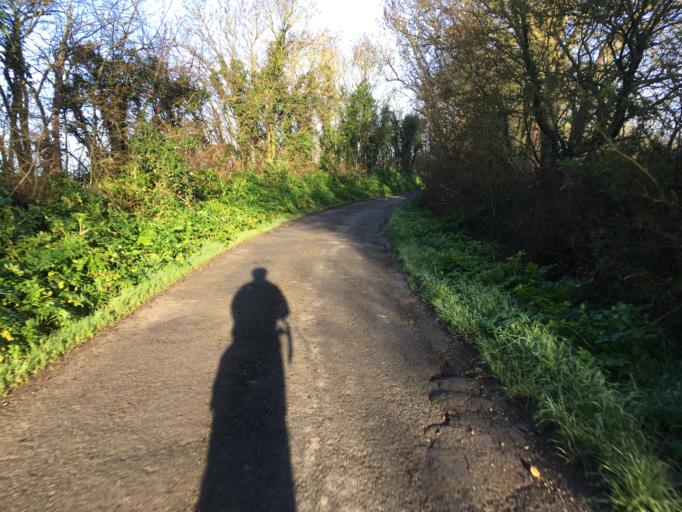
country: FR
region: Poitou-Charentes
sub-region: Departement de la Charente-Maritime
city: Nieul-sur-Mer
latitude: 46.1961
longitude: -1.1753
